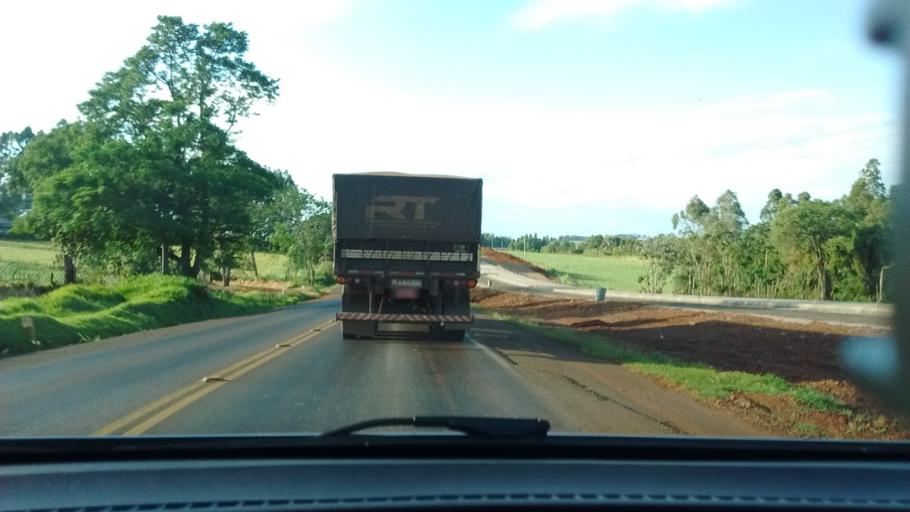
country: BR
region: Parana
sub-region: Cascavel
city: Cascavel
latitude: -25.1570
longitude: -53.5973
